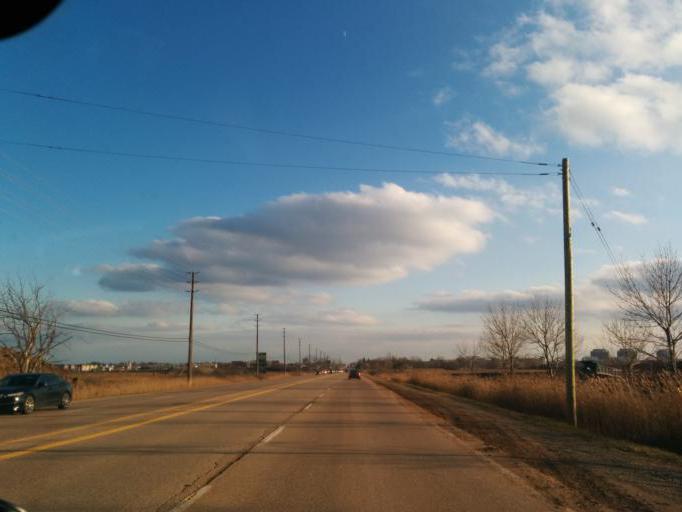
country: CA
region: Ontario
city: Oakville
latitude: 43.4937
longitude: -79.7274
